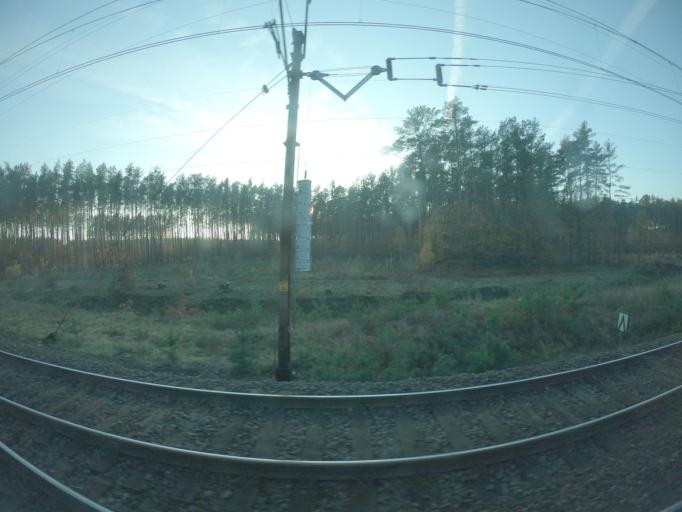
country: PL
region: Lubusz
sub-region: Powiat slubicki
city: Rzepin
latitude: 52.3093
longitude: 14.8641
